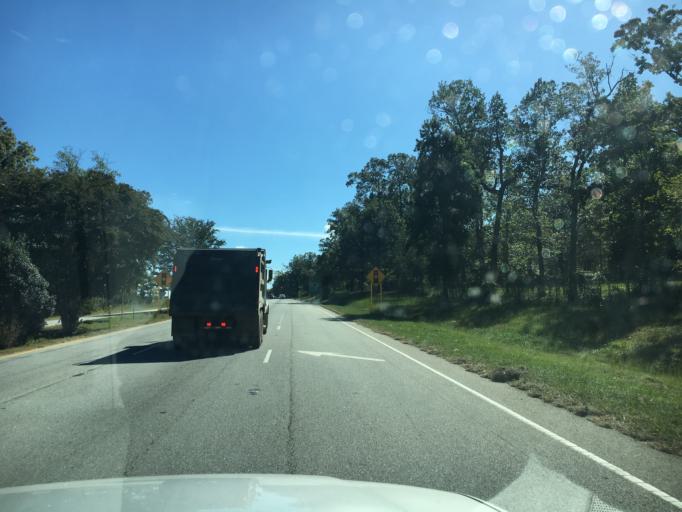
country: US
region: South Carolina
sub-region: Spartanburg County
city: Wellford
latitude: 34.9378
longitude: -82.0696
